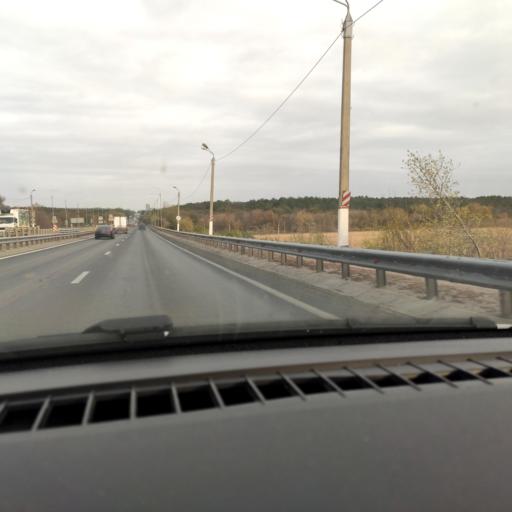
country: RU
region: Voronezj
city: Pridonskoy
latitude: 51.6498
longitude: 39.0750
